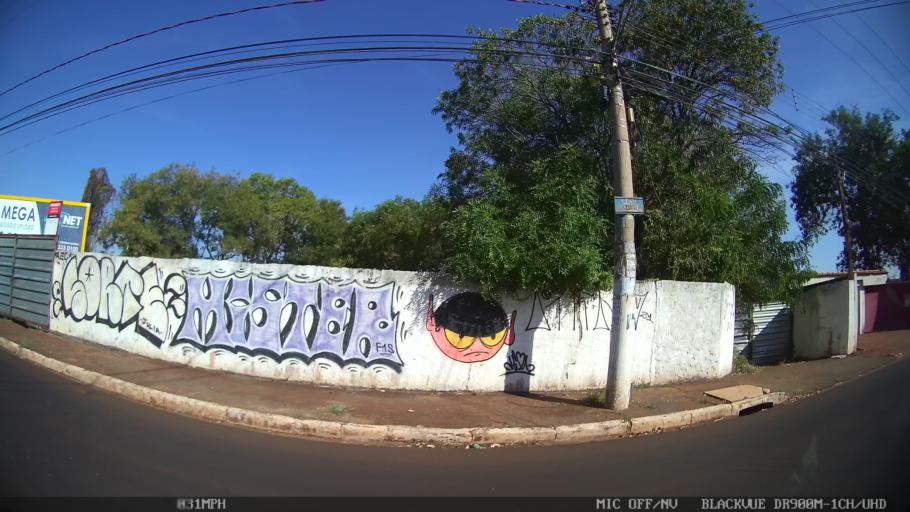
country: BR
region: Sao Paulo
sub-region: Ribeirao Preto
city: Ribeirao Preto
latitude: -21.1837
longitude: -47.7705
